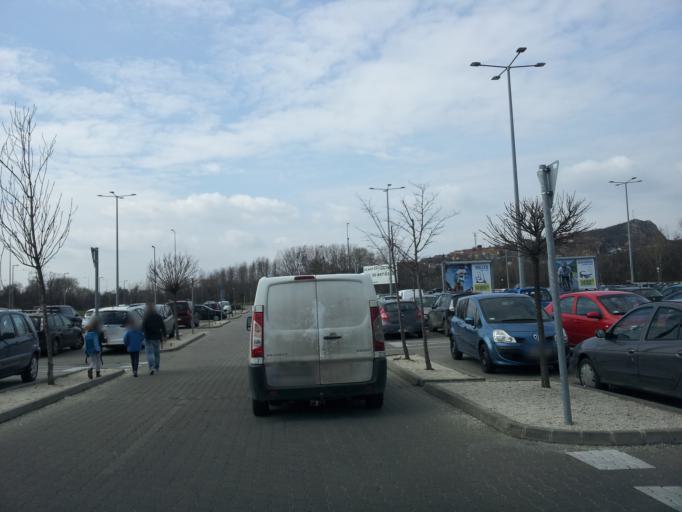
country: HU
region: Pest
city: Budaors
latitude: 47.4529
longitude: 18.9368
